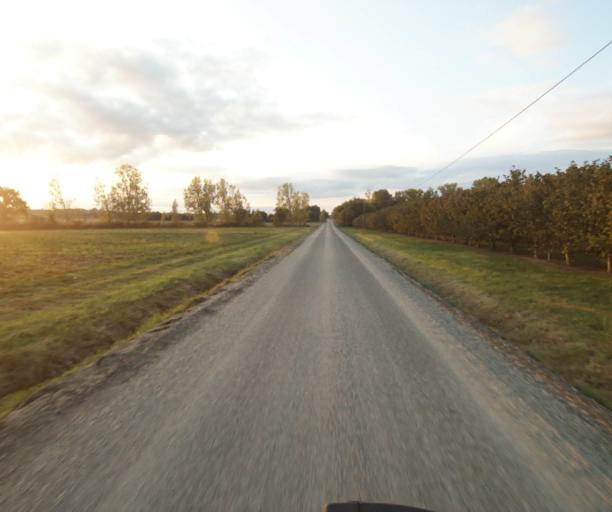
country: FR
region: Midi-Pyrenees
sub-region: Departement du Tarn-et-Garonne
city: Verdun-sur-Garonne
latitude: 43.8323
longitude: 1.2244
